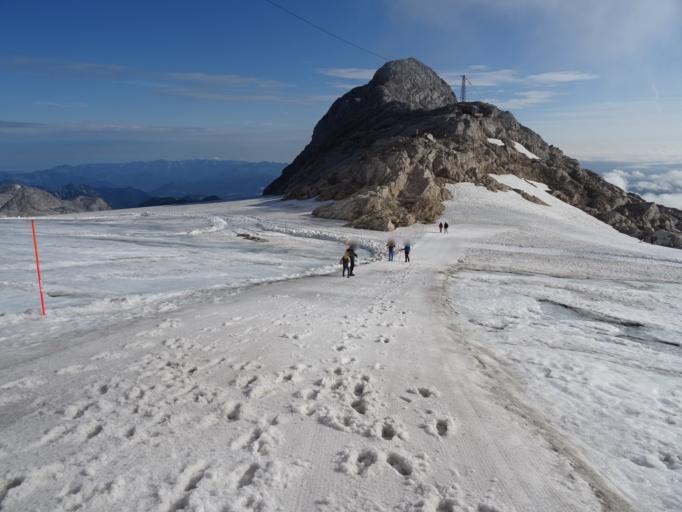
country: AT
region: Styria
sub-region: Politischer Bezirk Liezen
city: Schladming
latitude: 47.4709
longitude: 13.6249
